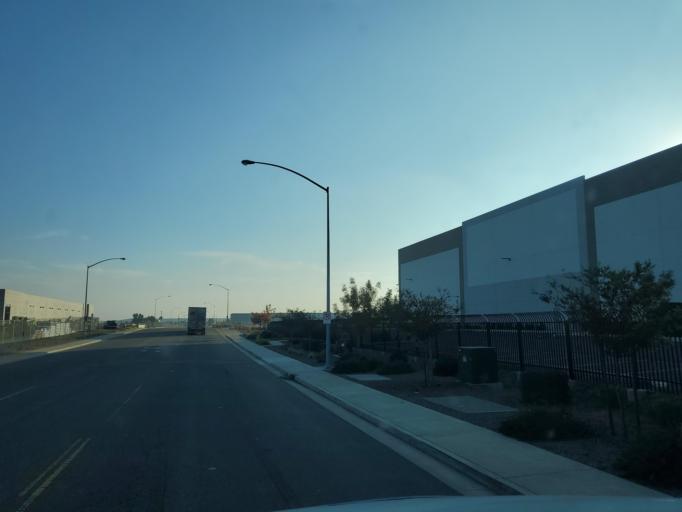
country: US
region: California
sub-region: San Joaquin County
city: Kennedy
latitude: 37.9099
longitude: -121.1932
